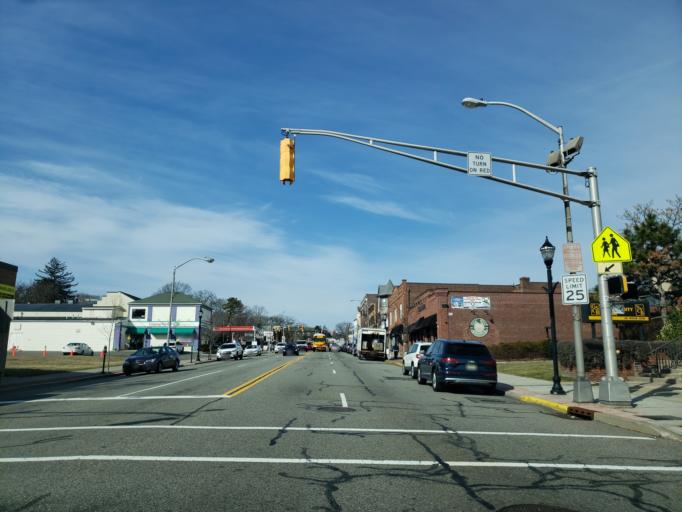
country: US
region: New Jersey
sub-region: Essex County
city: Verona
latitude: 40.8324
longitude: -74.2470
